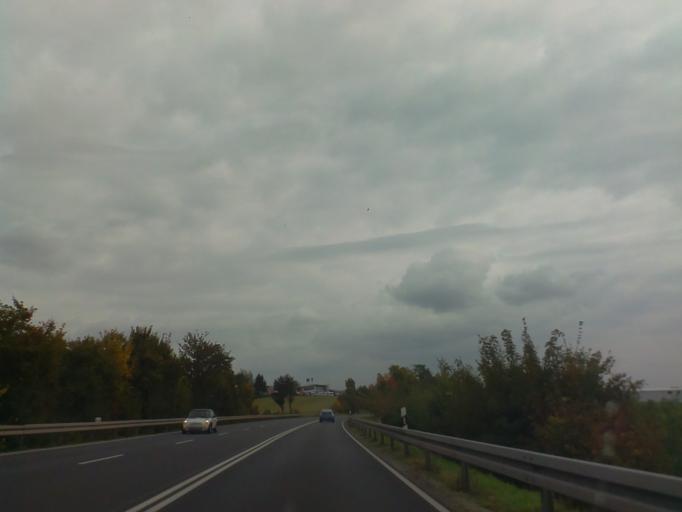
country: DE
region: Hesse
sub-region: Regierungsbezirk Kassel
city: Burghaun
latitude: 50.6948
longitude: 9.7437
